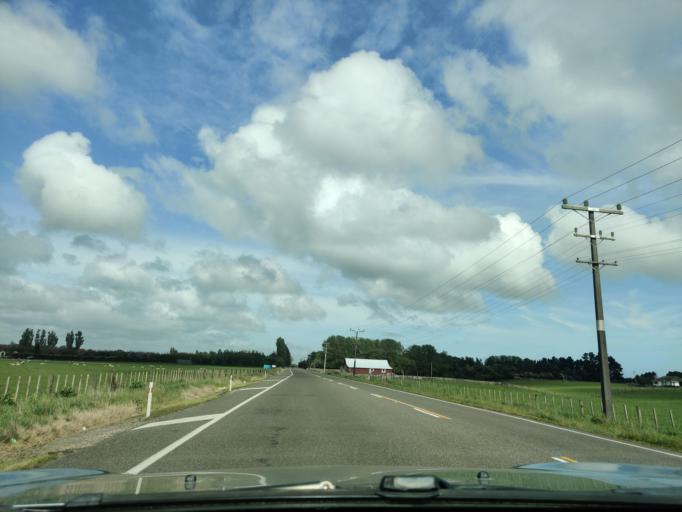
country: NZ
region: Manawatu-Wanganui
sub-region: Wanganui District
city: Wanganui
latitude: -39.8664
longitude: 174.9815
